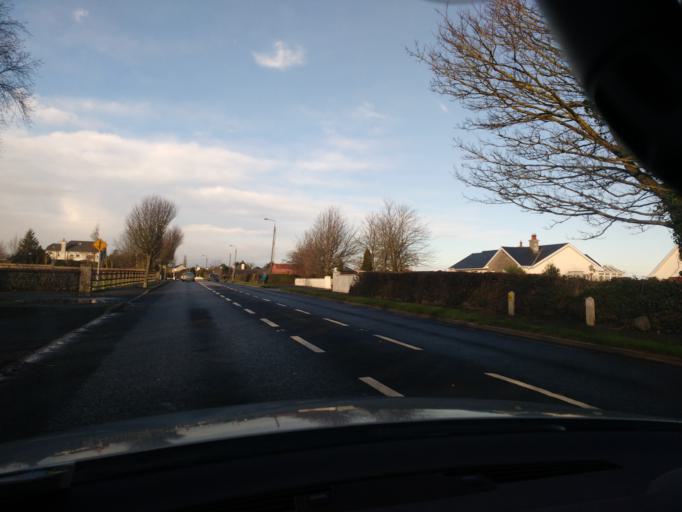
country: IE
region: Munster
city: Thurles
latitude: 52.6676
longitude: -7.8076
